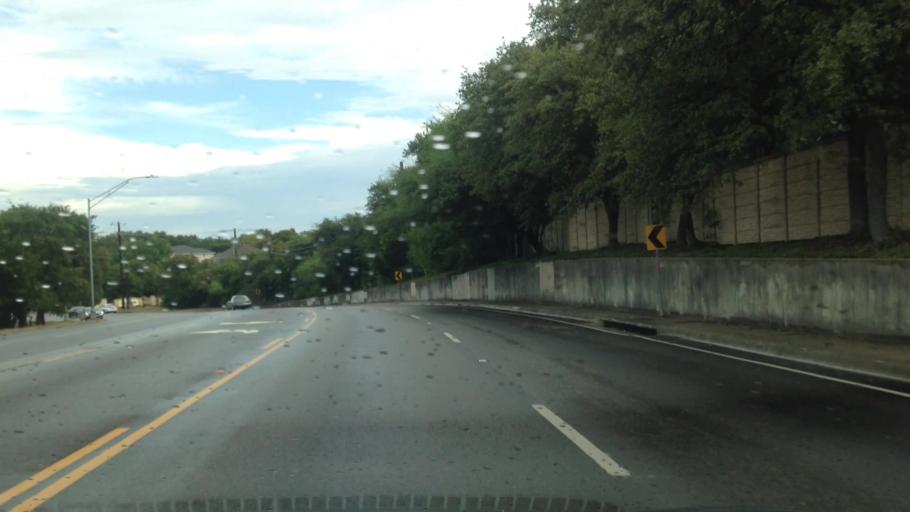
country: US
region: Texas
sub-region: Bexar County
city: Live Oak
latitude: 29.5942
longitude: -98.4016
